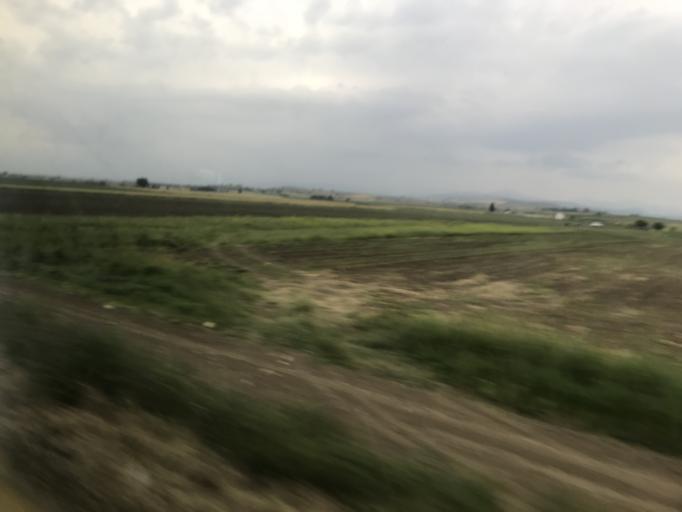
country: GR
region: East Macedonia and Thrace
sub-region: Nomos Rodopis
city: Aratos
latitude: 41.0830
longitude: 25.5447
